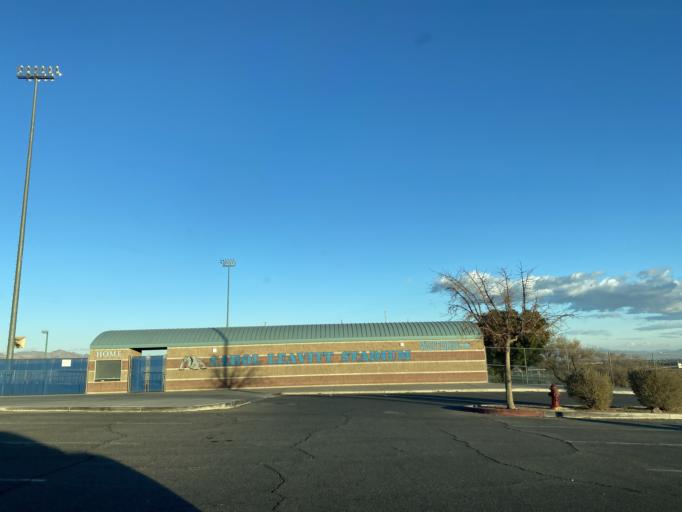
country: US
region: Nevada
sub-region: Clark County
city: Summerlin South
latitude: 36.2783
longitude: -115.3182
